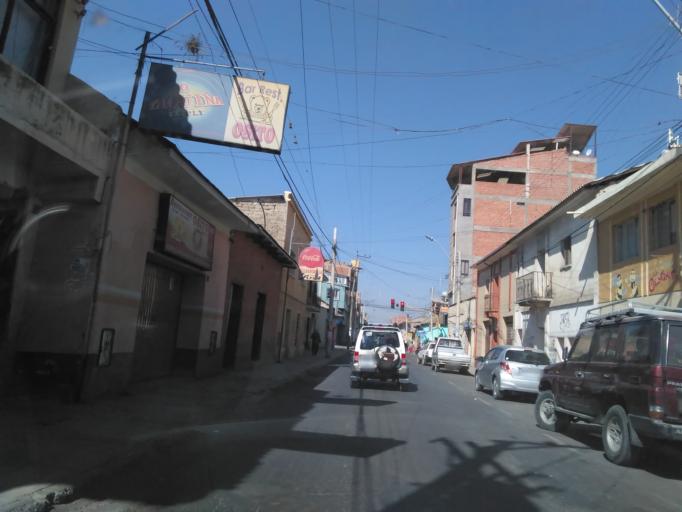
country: BO
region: Cochabamba
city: Sipe Sipe
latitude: -17.3983
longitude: -66.2793
